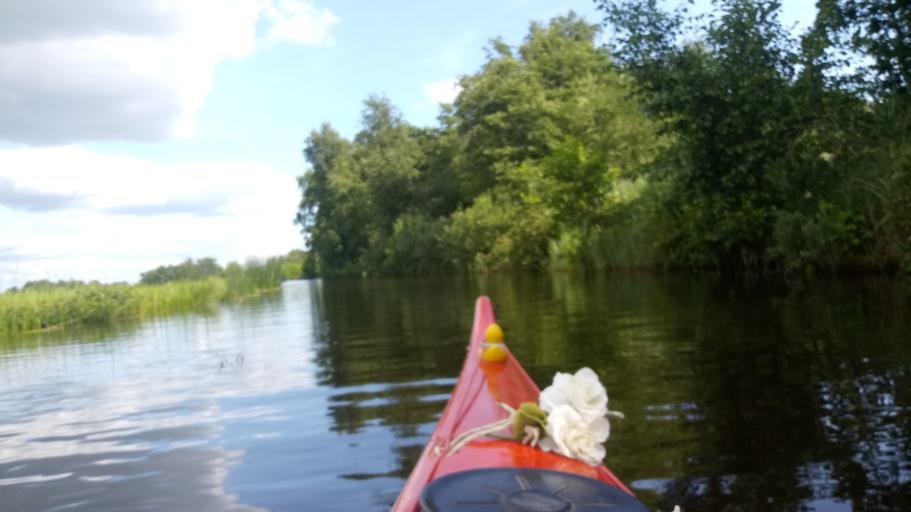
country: NL
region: Overijssel
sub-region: Gemeente Steenwijkerland
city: Wanneperveen
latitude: 52.7229
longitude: 6.1186
